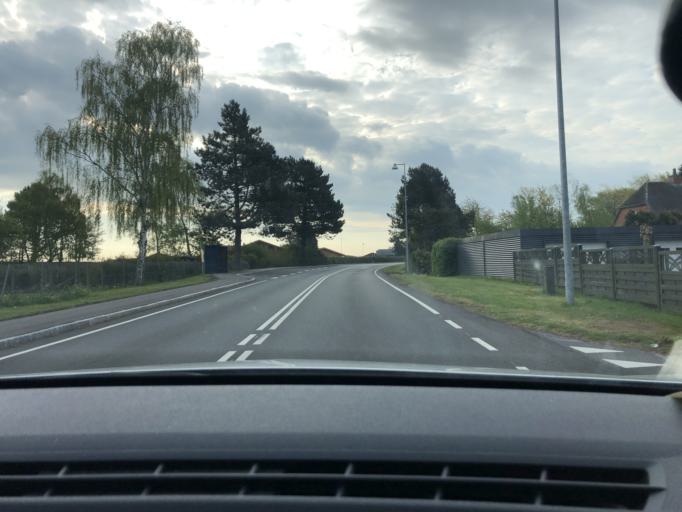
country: DK
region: Zealand
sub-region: Faxe Kommune
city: Ronnede
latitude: 55.2536
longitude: 12.0305
